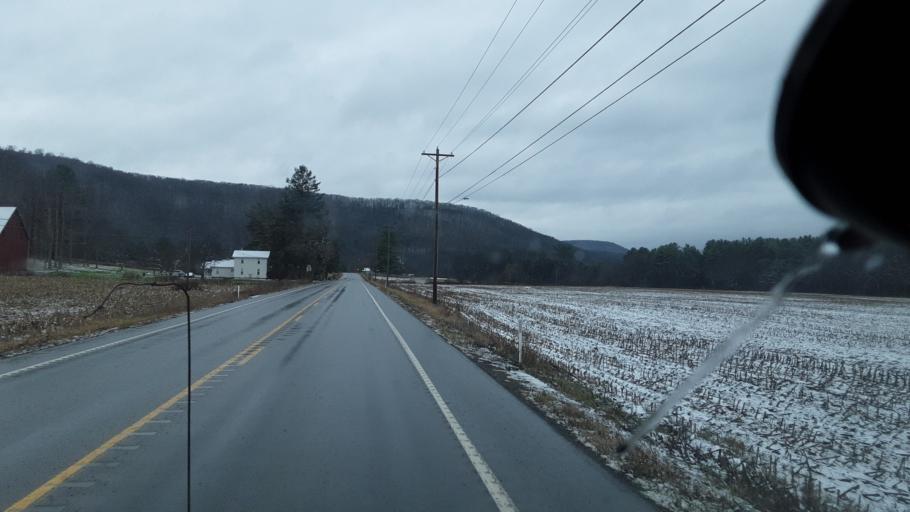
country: US
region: Pennsylvania
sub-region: Potter County
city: Coudersport
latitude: 41.9025
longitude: -78.0687
